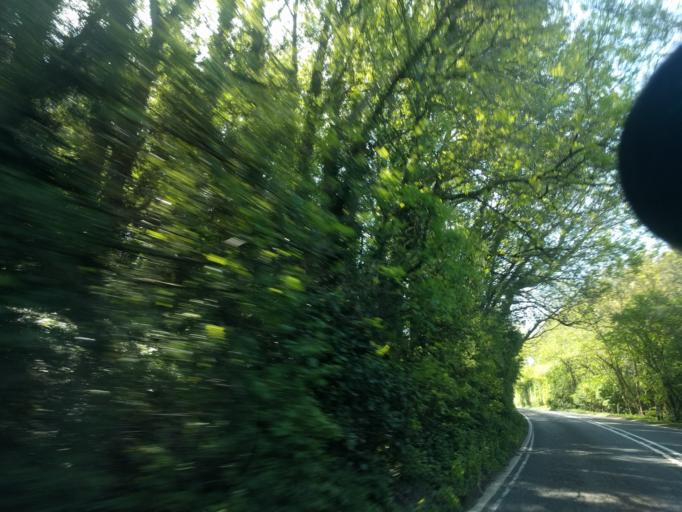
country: GB
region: England
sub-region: Somerset
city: Evercreech
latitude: 51.1388
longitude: -2.5514
